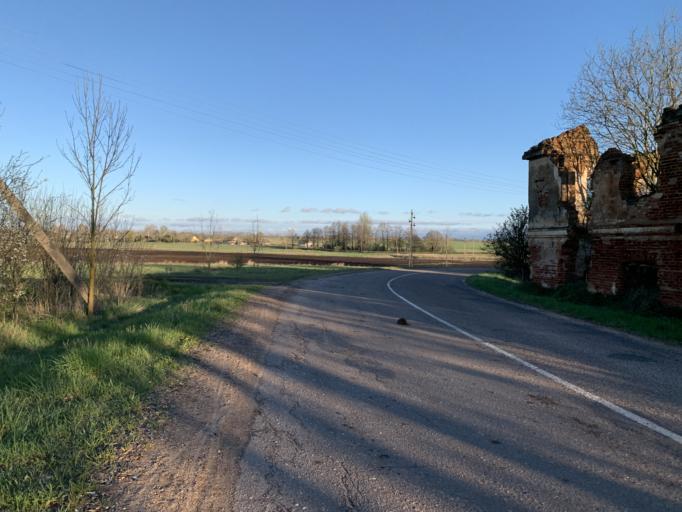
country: BY
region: Minsk
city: Haradzyeya
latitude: 53.3546
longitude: 26.5438
